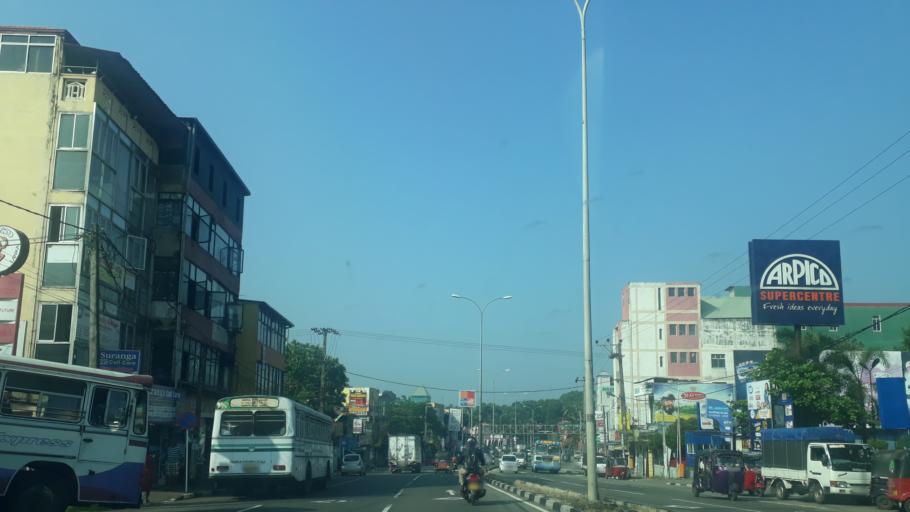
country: LK
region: Western
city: Kelaniya
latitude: 7.0013
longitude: 79.9503
